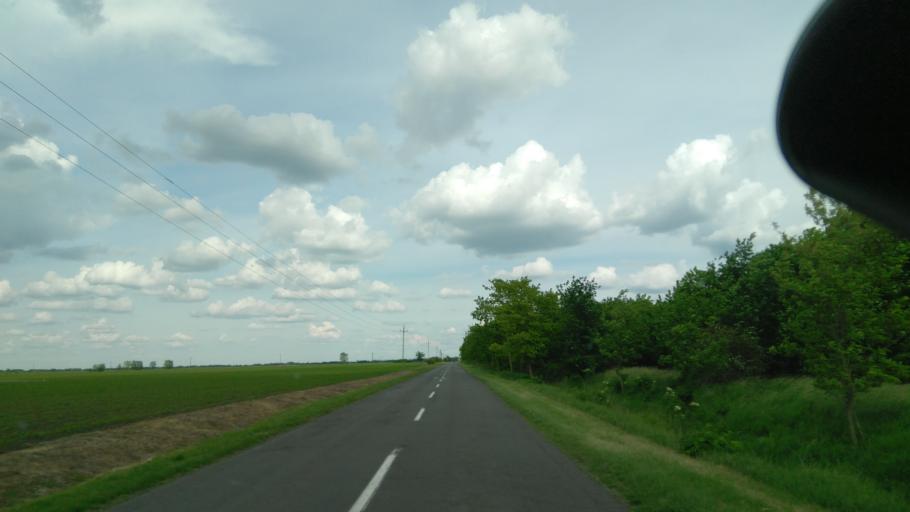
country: RO
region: Arad
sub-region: Comuna Peregu Mare
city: Peregu Mic
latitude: 46.3008
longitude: 20.9301
